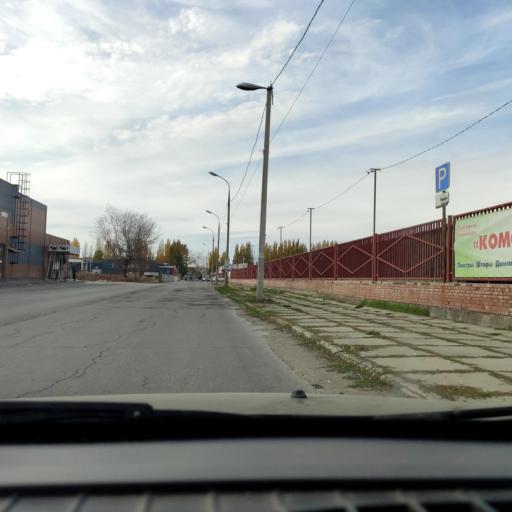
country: RU
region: Samara
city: Tol'yatti
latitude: 53.5399
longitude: 49.2834
